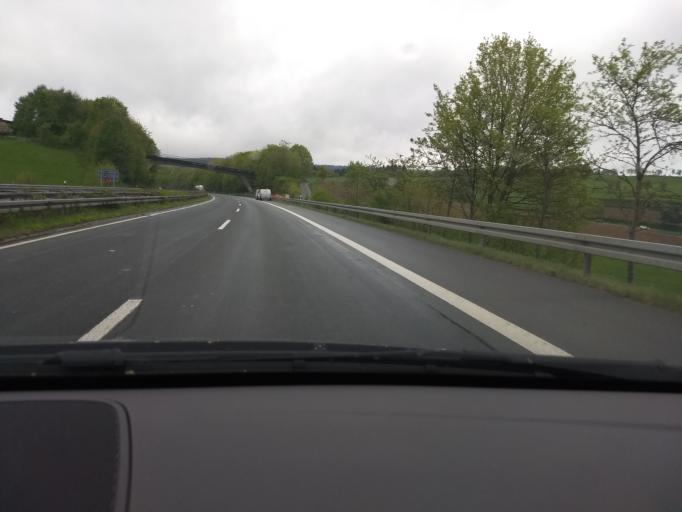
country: DE
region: North Rhine-Westphalia
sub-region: Regierungsbezirk Arnsberg
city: Meschede
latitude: 51.3638
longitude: 8.3254
